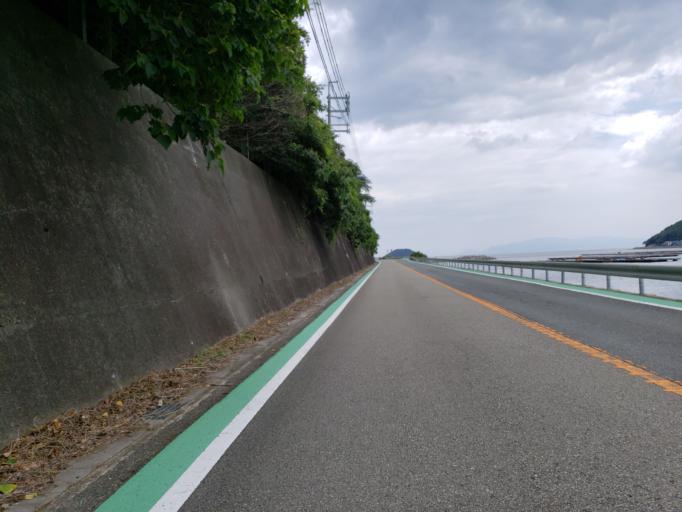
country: JP
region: Hyogo
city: Aioi
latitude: 34.7712
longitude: 134.4701
